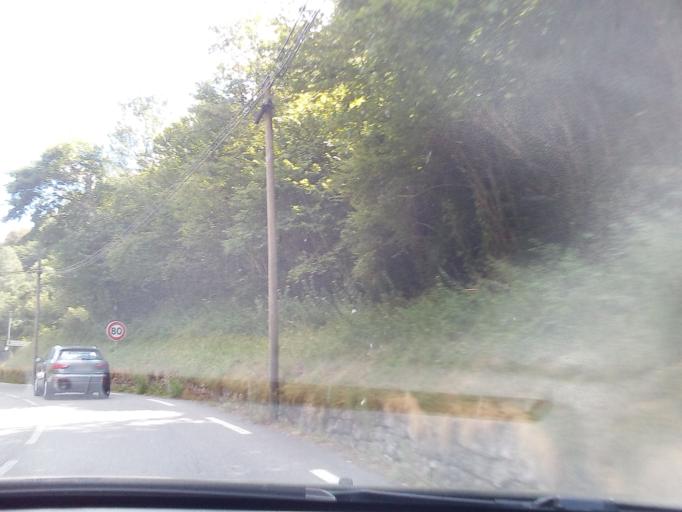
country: FR
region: Aquitaine
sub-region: Departement des Pyrenees-Atlantiques
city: Laruns
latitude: 42.8846
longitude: -0.5628
